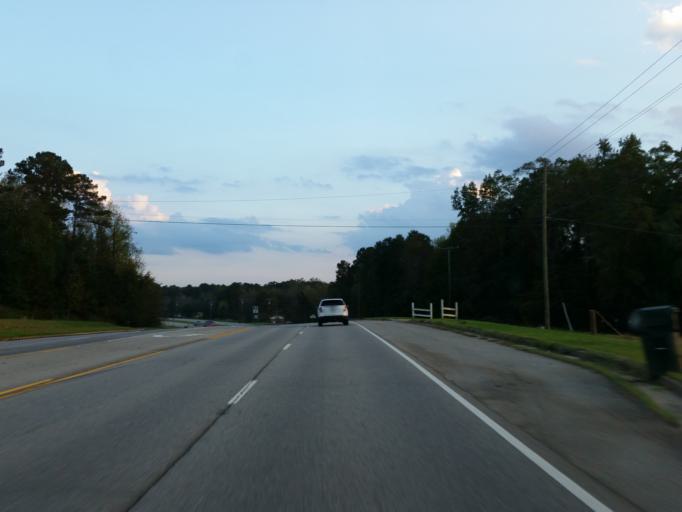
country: US
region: Georgia
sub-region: Houston County
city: Perry
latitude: 32.3740
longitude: -83.6180
